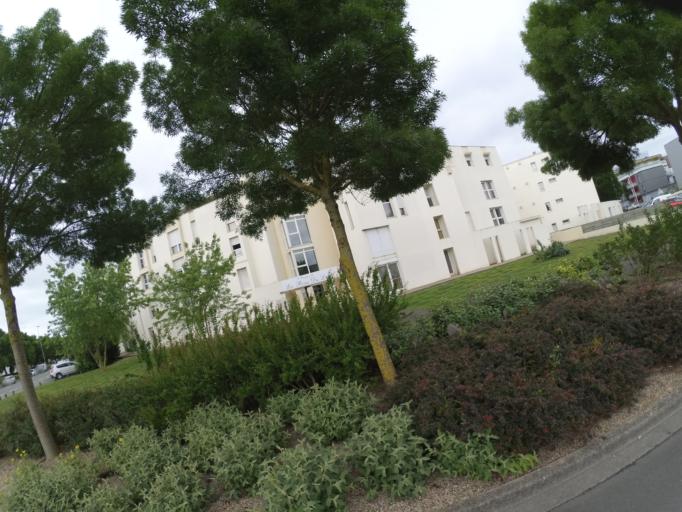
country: FR
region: Poitou-Charentes
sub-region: Departement de la Charente-Maritime
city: La Rochelle
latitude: 46.1459
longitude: -1.1527
